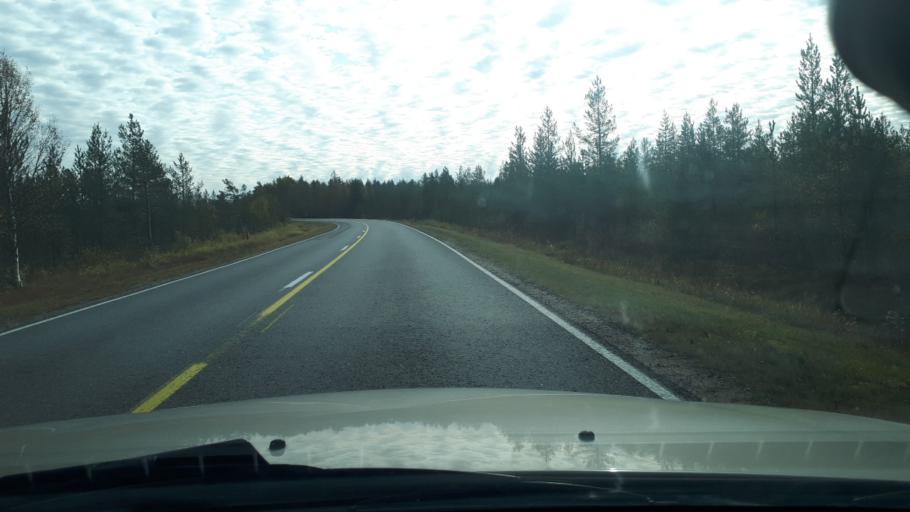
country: FI
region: Lapland
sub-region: Rovaniemi
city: Ranua
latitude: 65.9638
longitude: 26.0259
